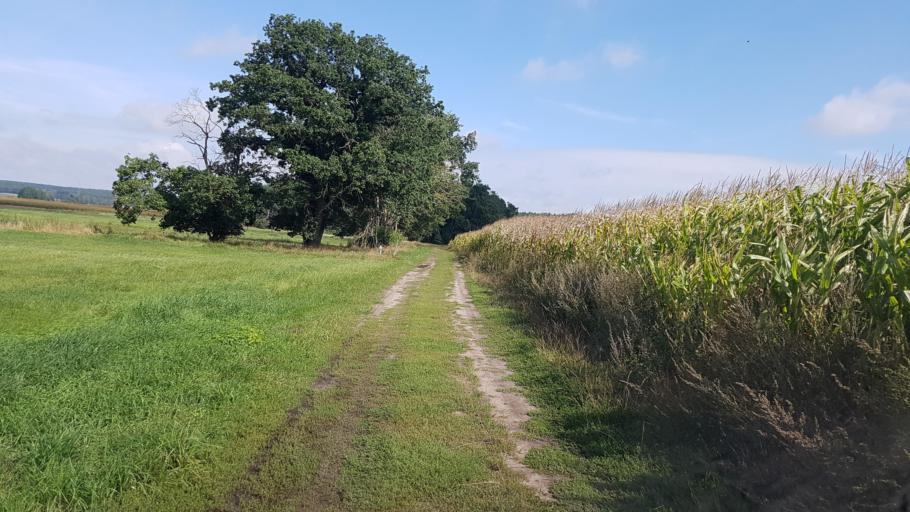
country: DE
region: Brandenburg
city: Hohenbucko
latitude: 51.7184
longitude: 13.4821
